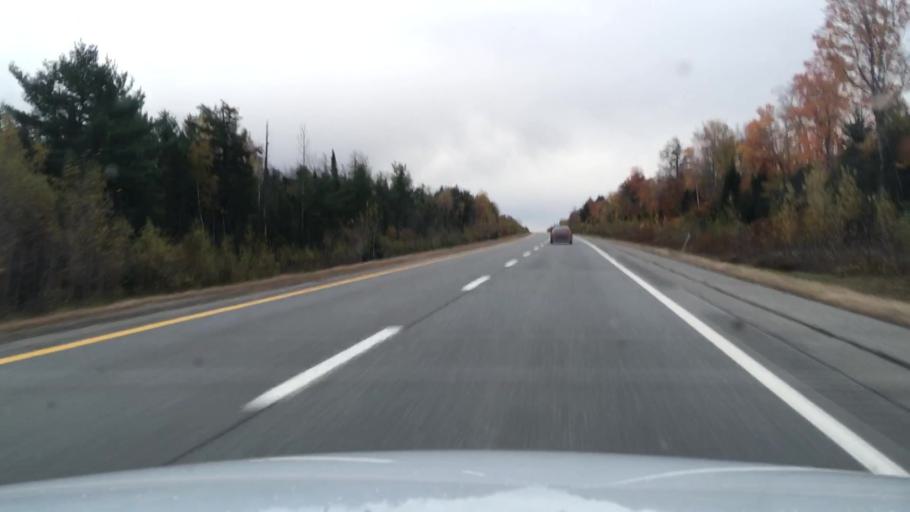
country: US
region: Maine
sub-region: Penobscot County
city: Greenbush
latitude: 45.0954
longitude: -68.6959
